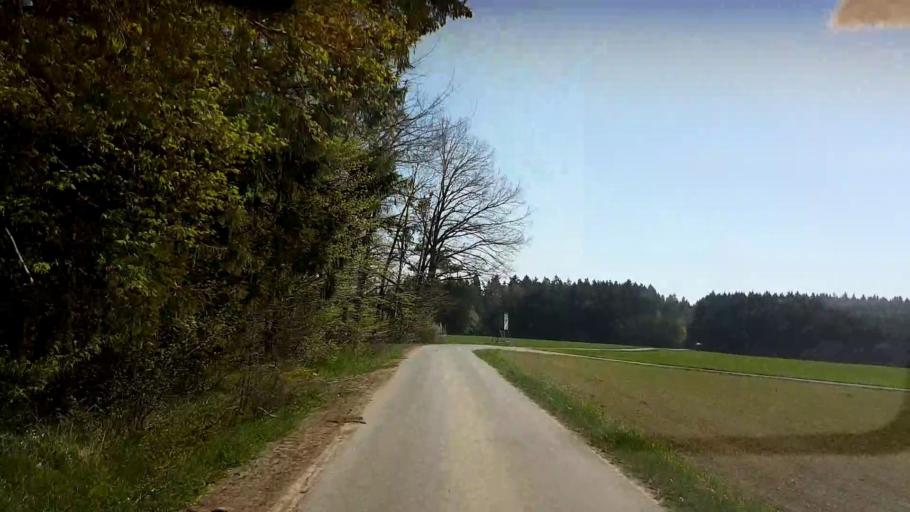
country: DE
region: Bavaria
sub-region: Upper Franconia
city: Konigsfeld
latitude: 49.9222
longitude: 11.1747
